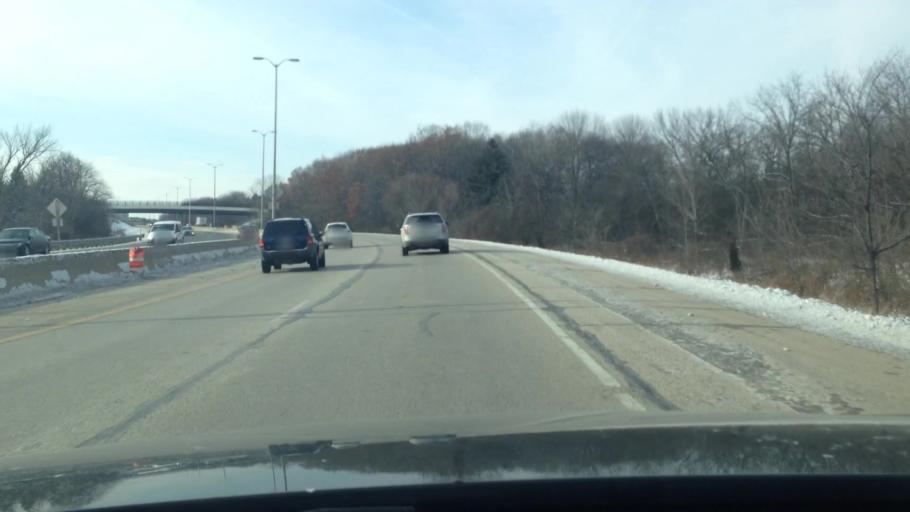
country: US
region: Wisconsin
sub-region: Milwaukee County
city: Hales Corners
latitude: 42.9574
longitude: -88.0535
